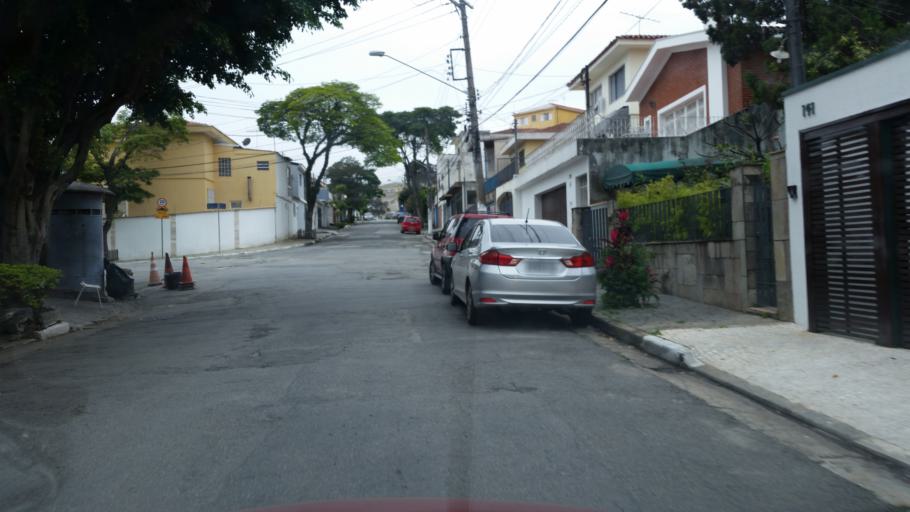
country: BR
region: Sao Paulo
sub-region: Diadema
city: Diadema
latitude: -23.6373
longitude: -46.6592
